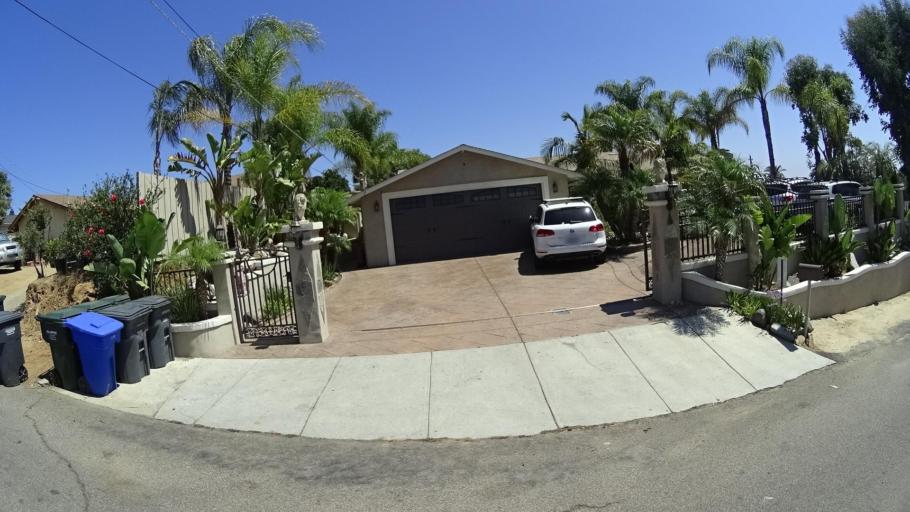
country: US
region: California
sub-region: San Diego County
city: Fallbrook
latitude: 33.3778
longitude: -117.2579
